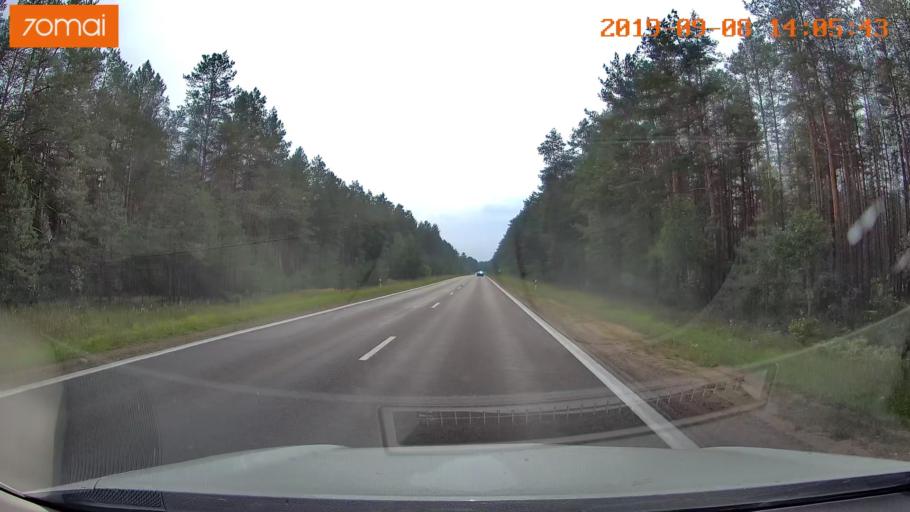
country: LT
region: Alytaus apskritis
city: Druskininkai
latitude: 54.0792
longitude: 24.1935
